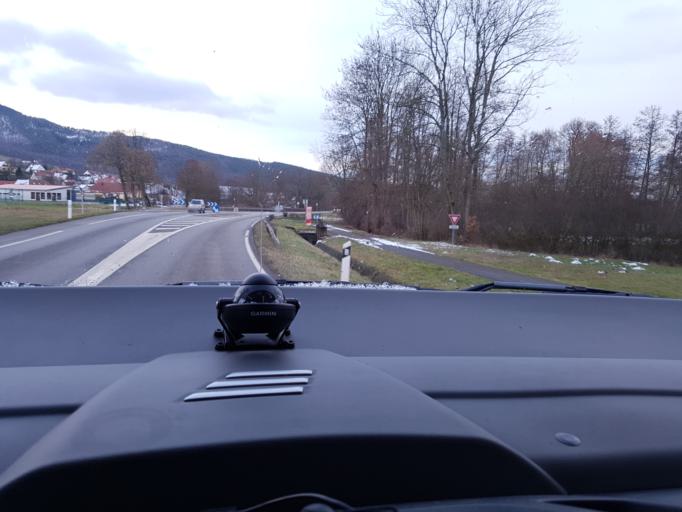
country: FR
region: Alsace
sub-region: Departement du Bas-Rhin
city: Ville
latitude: 48.3217
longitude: 7.3455
